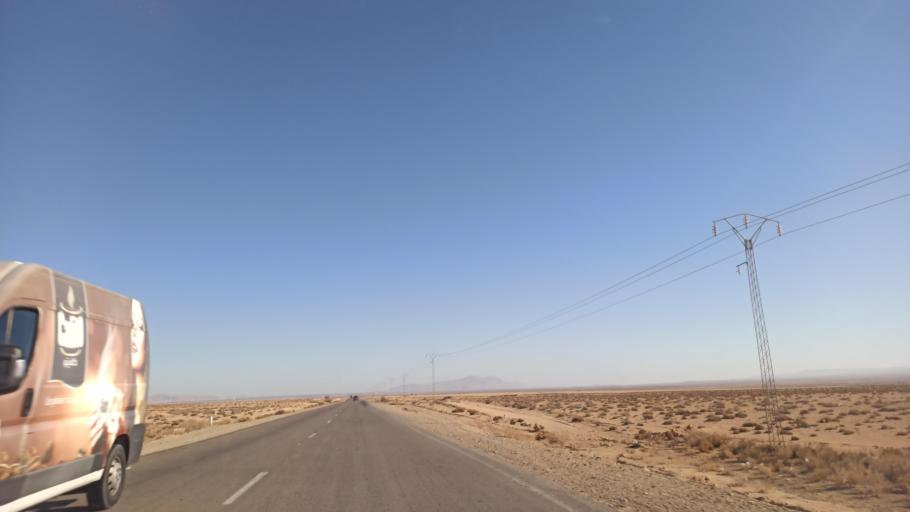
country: TN
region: Gafsa
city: Al Metlaoui
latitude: 34.3221
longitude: 8.5248
